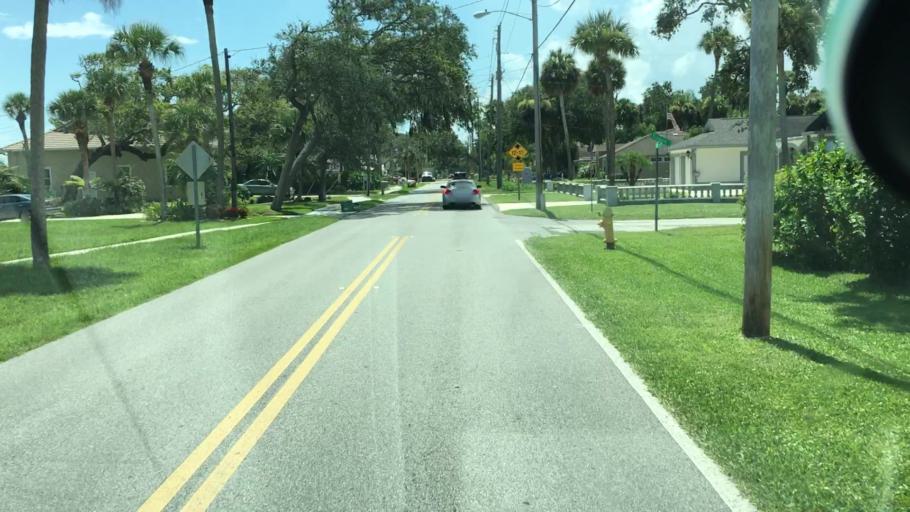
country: US
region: Florida
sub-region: Volusia County
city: Holly Hill
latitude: 29.2602
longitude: -81.0426
